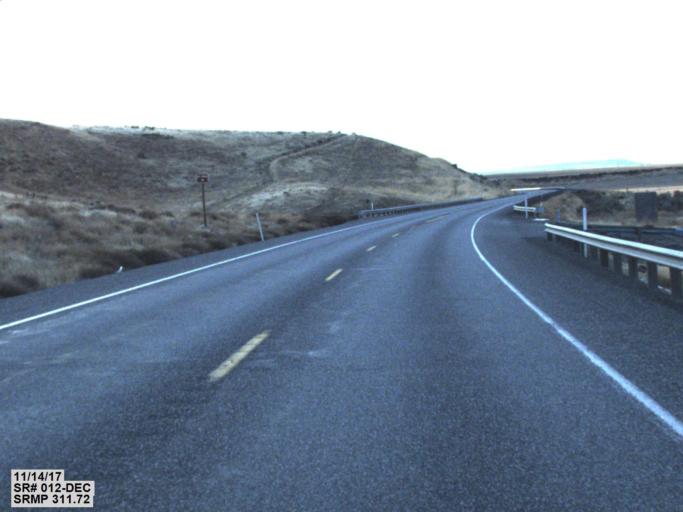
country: US
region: Washington
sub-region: Benton County
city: Finley
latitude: 46.0659
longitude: -118.8286
